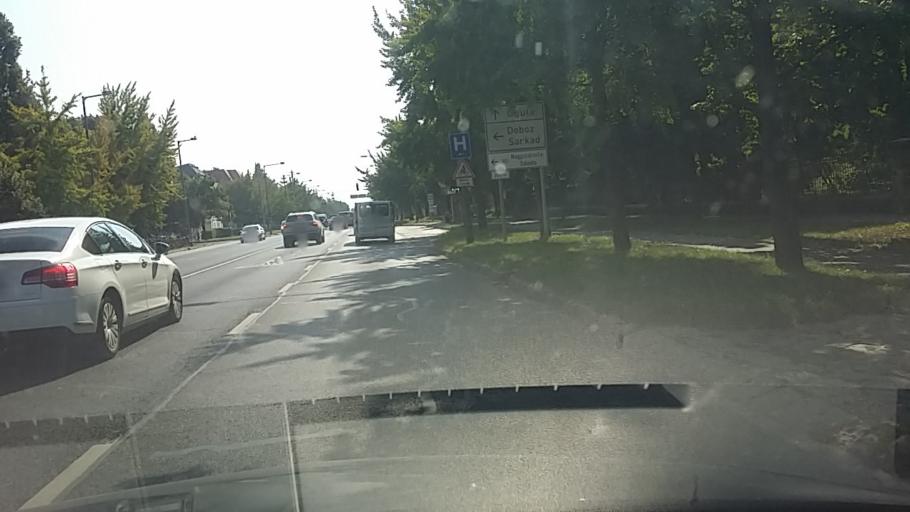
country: HU
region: Bekes
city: Bekescsaba
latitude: 46.6820
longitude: 21.1028
